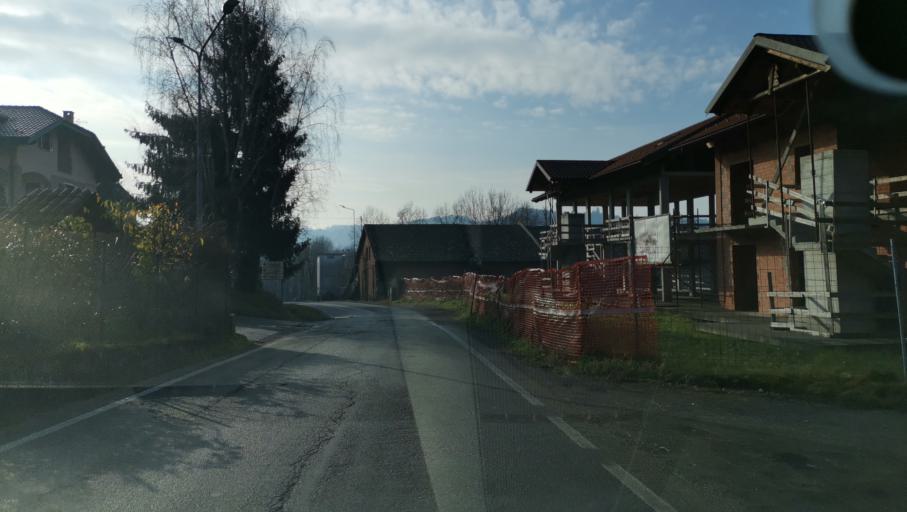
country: IT
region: Piedmont
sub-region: Provincia di Torino
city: Rivalba
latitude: 45.1166
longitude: 7.8880
